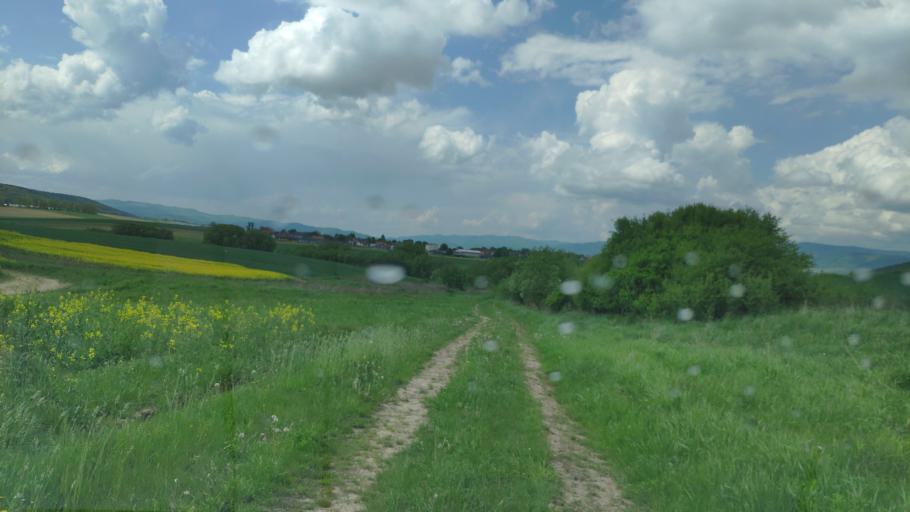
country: SK
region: Presovsky
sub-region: Okres Presov
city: Presov
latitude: 49.0327
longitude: 21.1648
